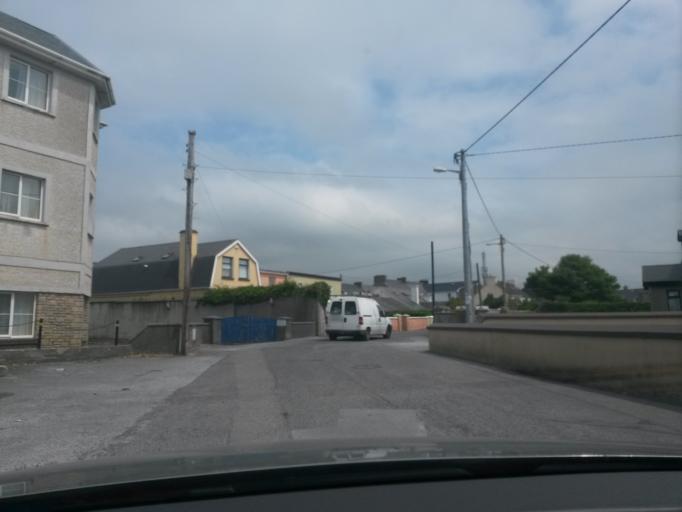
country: IE
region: Munster
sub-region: Ciarrai
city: Ballybunnion
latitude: 52.5108
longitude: -9.6735
